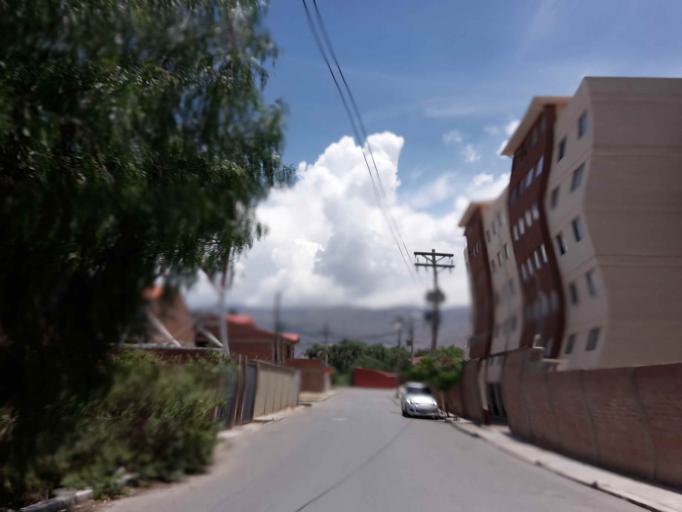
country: BO
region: Cochabamba
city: Cochabamba
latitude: -17.3766
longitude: -66.1991
